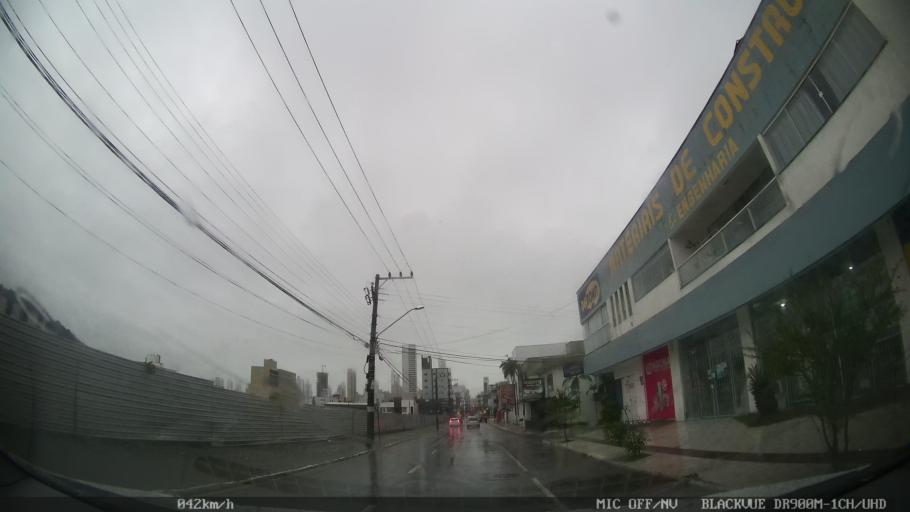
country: BR
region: Santa Catarina
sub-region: Balneario Camboriu
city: Balneario Camboriu
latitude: -26.9956
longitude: -48.6431
